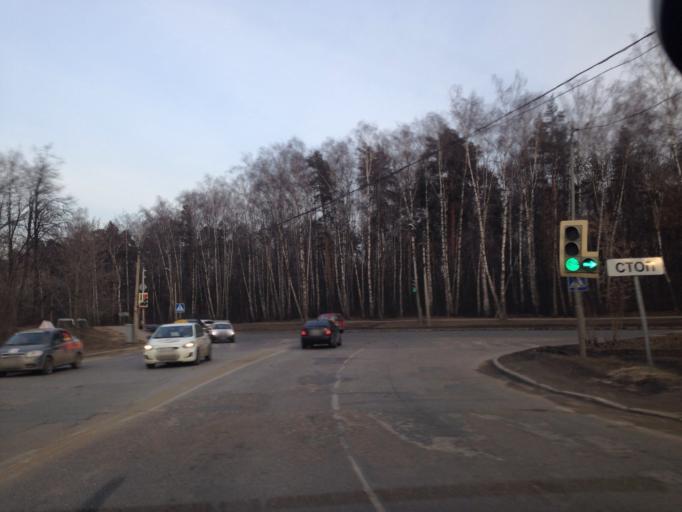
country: RU
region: Moskovskaya
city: Balashikha
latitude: 55.8061
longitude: 37.9407
